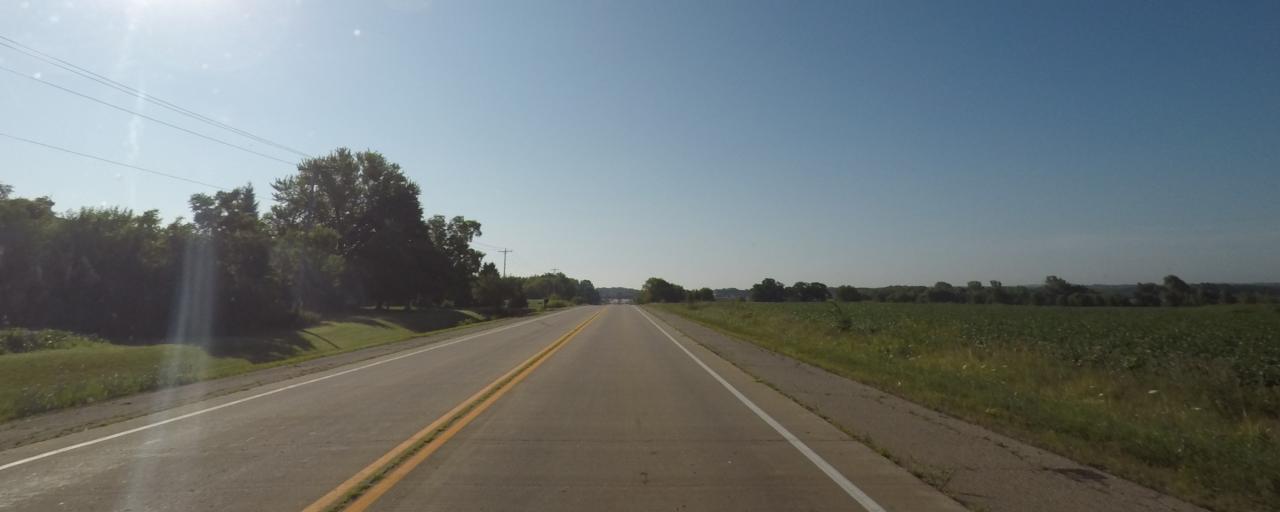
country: US
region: Wisconsin
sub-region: Jefferson County
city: Fort Atkinson
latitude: 42.9479
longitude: -88.8745
